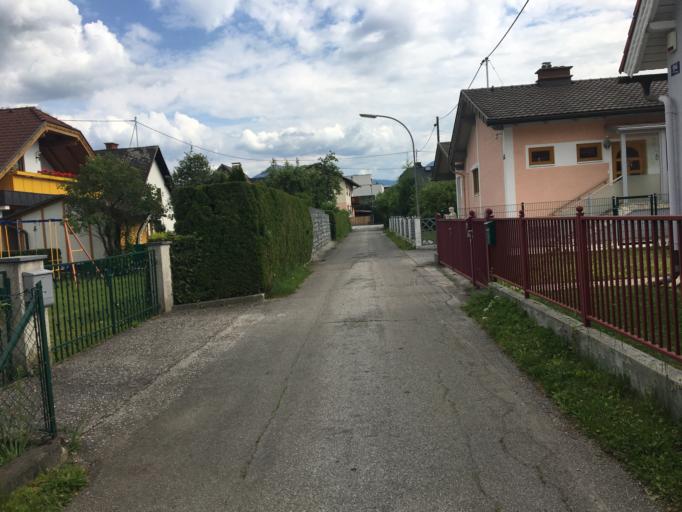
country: AT
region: Carinthia
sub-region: Klagenfurt am Woerthersee
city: Klagenfurt am Woerthersee
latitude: 46.5976
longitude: 14.2727
